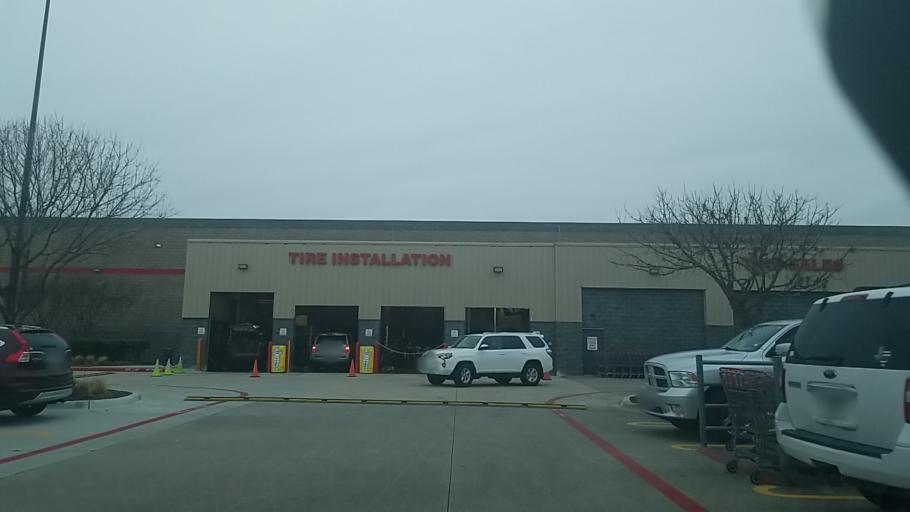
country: US
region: Texas
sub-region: Denton County
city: Lewisville
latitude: 32.9977
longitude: -96.9648
